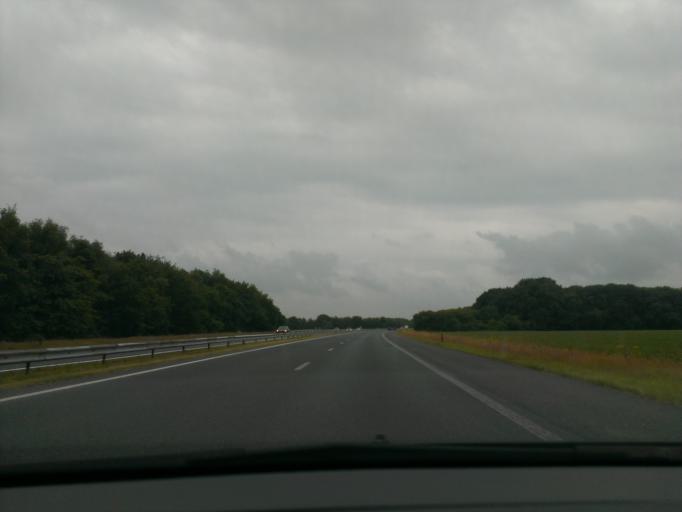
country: NL
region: Drenthe
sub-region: Gemeente Tynaarlo
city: Tynaarlo
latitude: 53.1009
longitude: 6.6123
